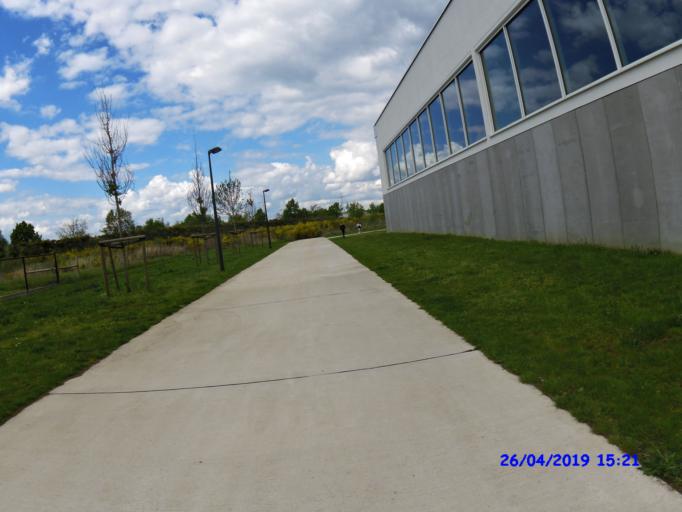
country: BE
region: Flanders
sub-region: Provincie Limburg
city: Beringen
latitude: 51.0526
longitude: 5.2195
